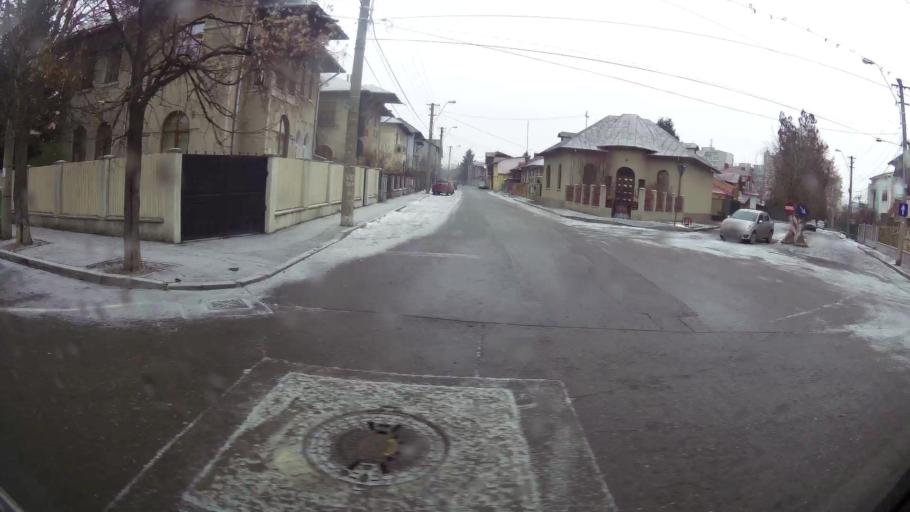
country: RO
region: Prahova
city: Ploiesti
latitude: 44.9430
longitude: 26.0332
